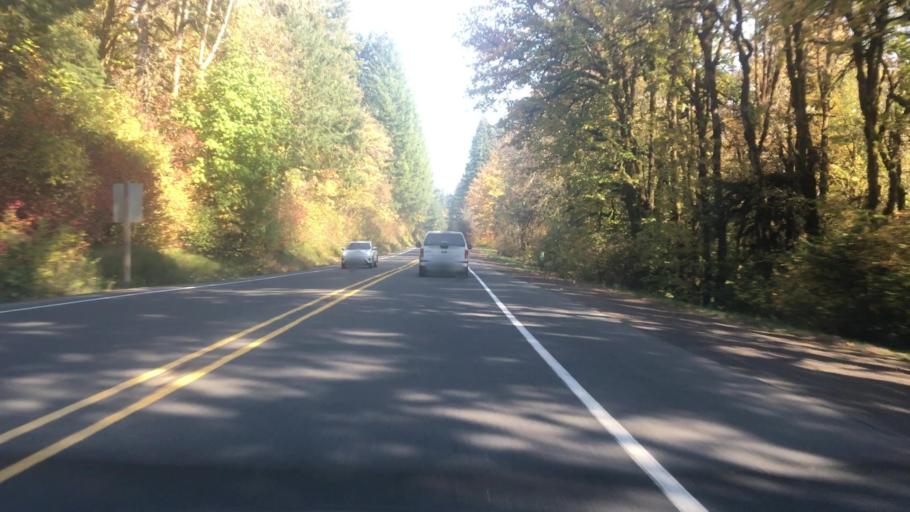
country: US
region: Oregon
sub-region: Polk County
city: Grand Ronde
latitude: 45.0595
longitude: -123.6753
